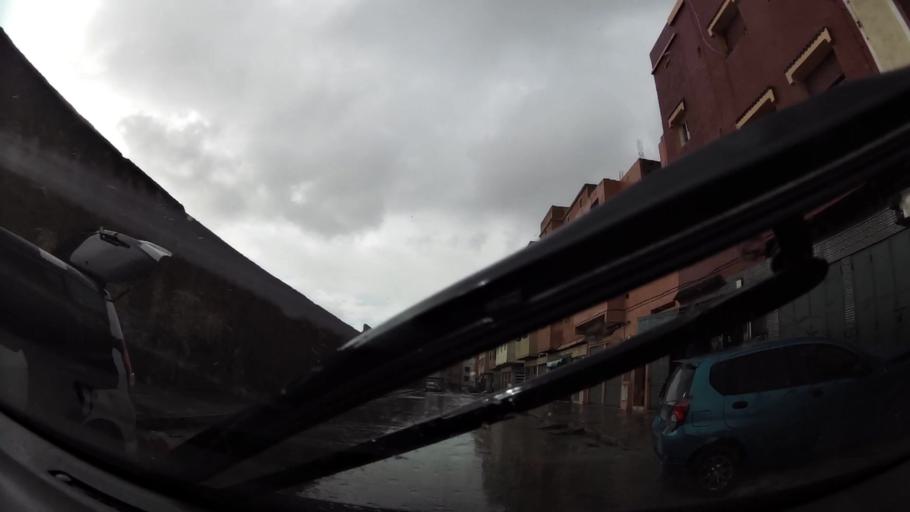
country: MA
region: Grand Casablanca
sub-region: Casablanca
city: Casablanca
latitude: 33.5475
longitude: -7.5865
